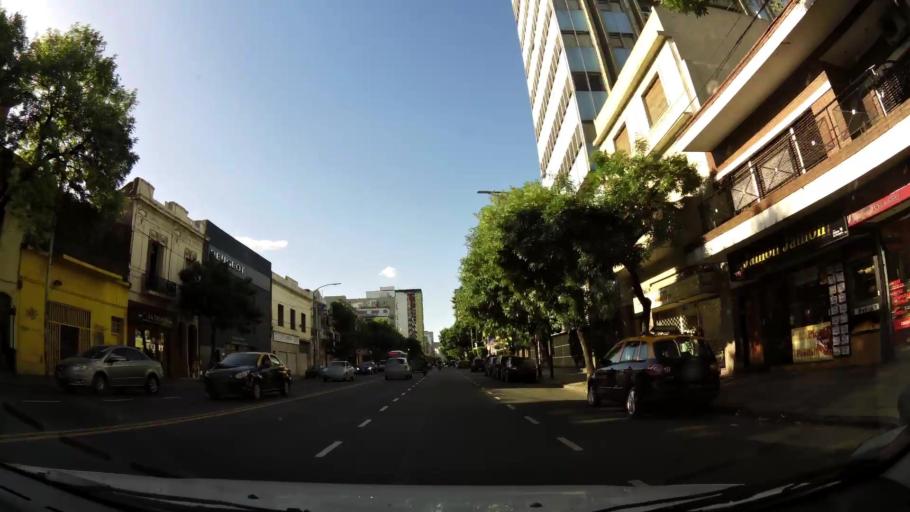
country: AR
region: Buenos Aires F.D.
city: Buenos Aires
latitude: -34.6248
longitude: -58.4272
